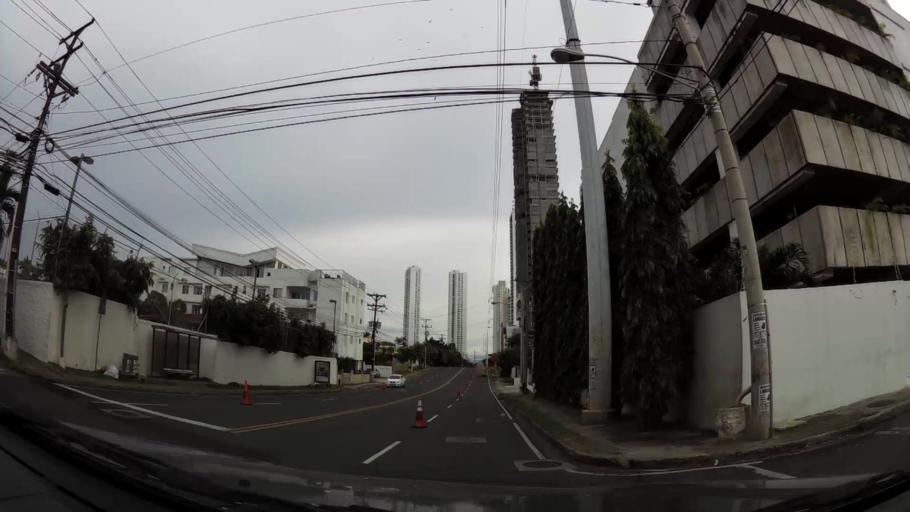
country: PA
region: Panama
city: Panama
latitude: 8.9993
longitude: -79.4975
